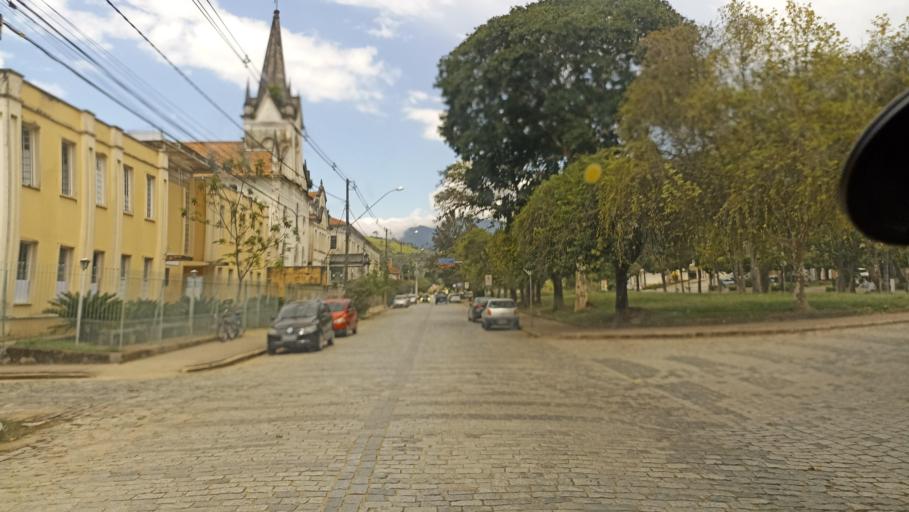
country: BR
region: Minas Gerais
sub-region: Passa Quatro
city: Passa Quatro
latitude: -22.3852
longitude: -44.9659
